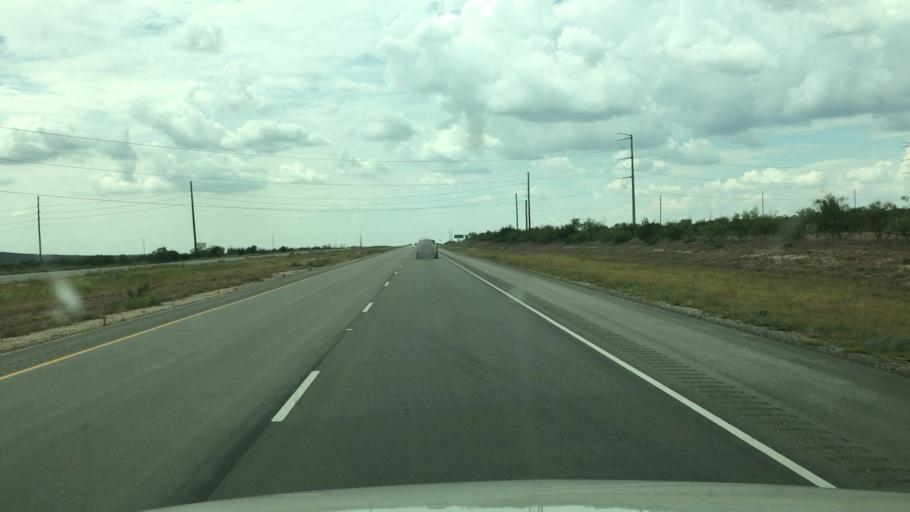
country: US
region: Texas
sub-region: Glasscock County
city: Garden City
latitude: 31.9871
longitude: -101.2634
